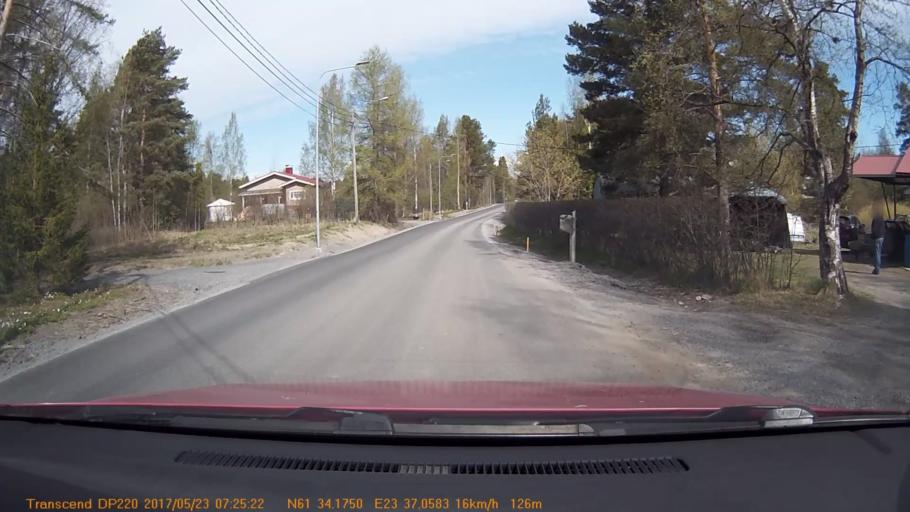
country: FI
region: Pirkanmaa
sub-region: Tampere
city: Yloejaervi
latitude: 61.5695
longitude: 23.6177
